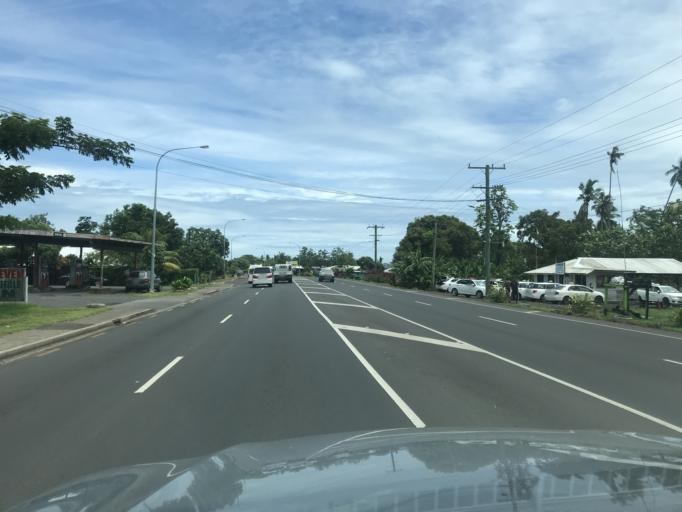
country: WS
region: Tuamasaga
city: Vaiusu
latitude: -13.8302
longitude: -171.7919
